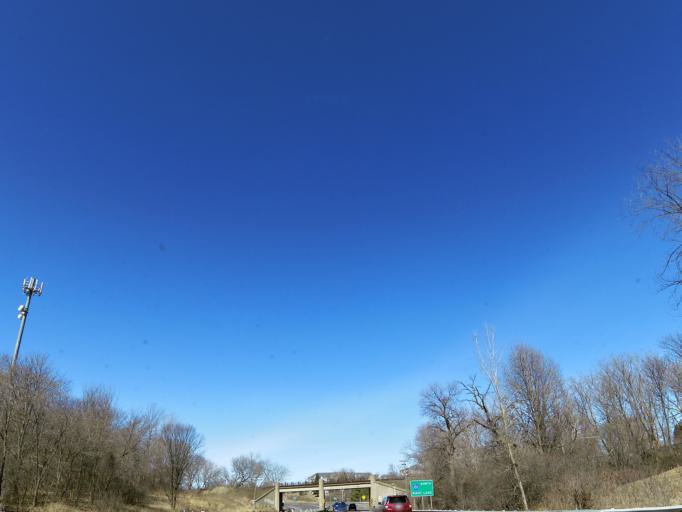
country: US
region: Minnesota
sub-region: Hennepin County
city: Corcoran
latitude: 45.0405
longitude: -93.5194
